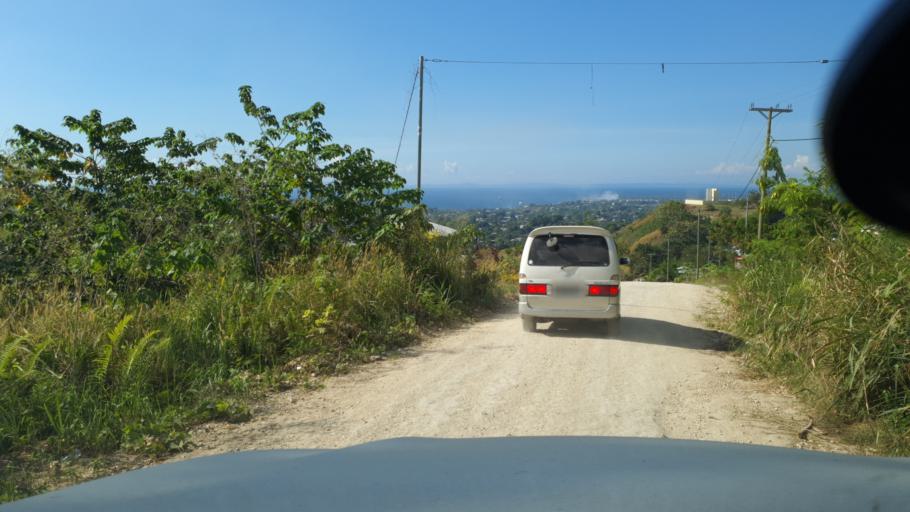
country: SB
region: Guadalcanal
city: Honiara
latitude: -9.4577
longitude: 159.9772
